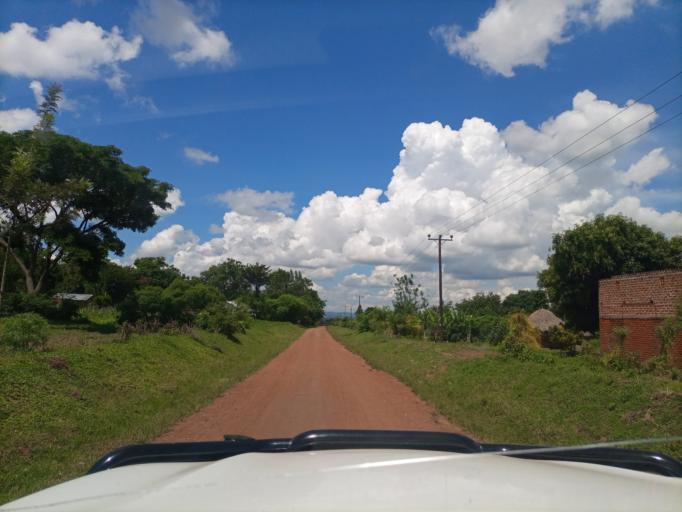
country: UG
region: Eastern Region
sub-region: Tororo District
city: Tororo
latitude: 0.6915
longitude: 34.0103
